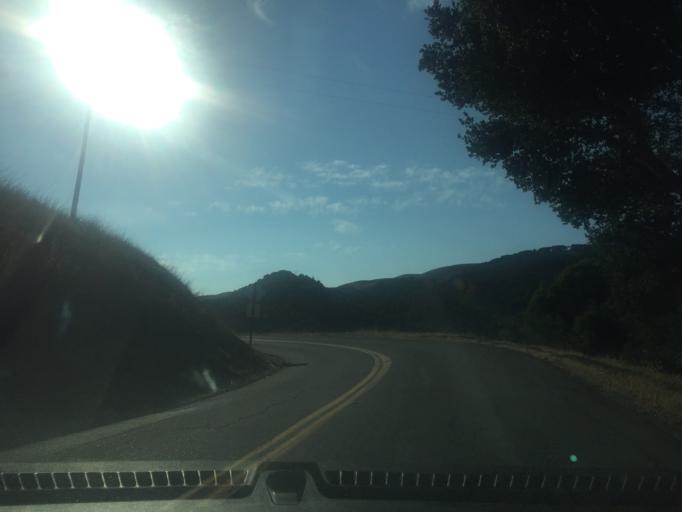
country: US
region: California
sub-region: Santa Barbara County
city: Lompoc
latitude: 34.5153
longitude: -120.4598
